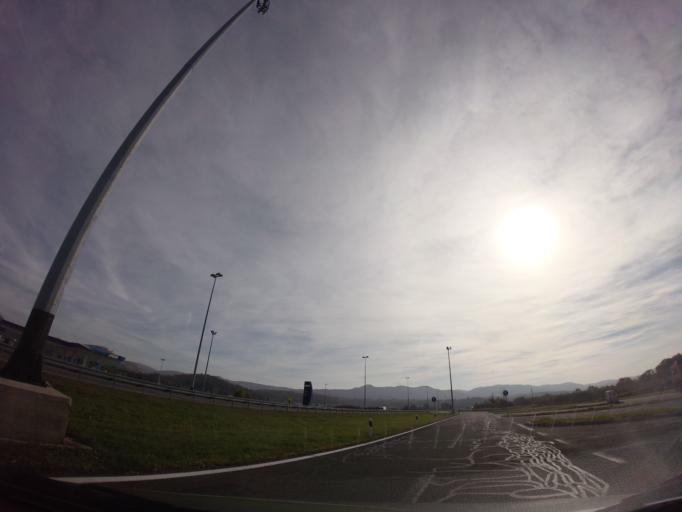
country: HR
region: Varazdinska
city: Ljubescica
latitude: 46.1686
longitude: 16.3746
